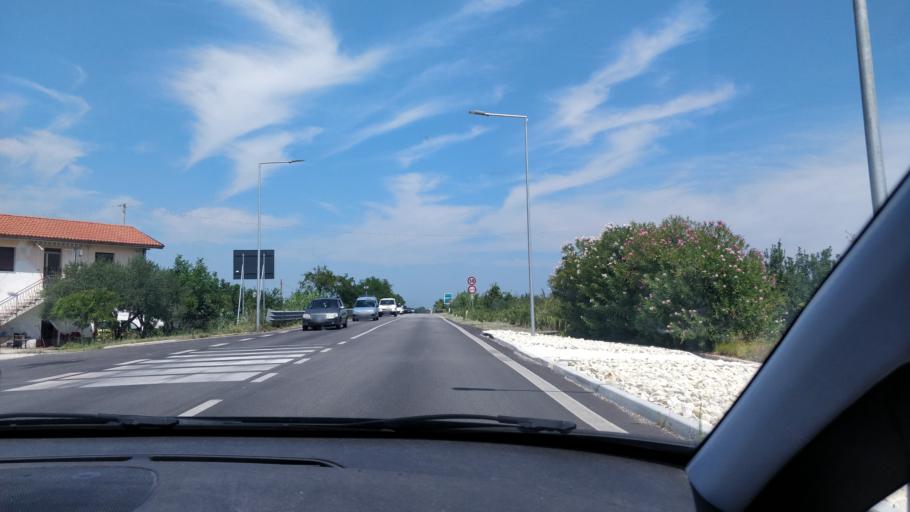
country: IT
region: Abruzzo
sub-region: Provincia di Chieti
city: Ortona
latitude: 42.3621
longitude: 14.3830
